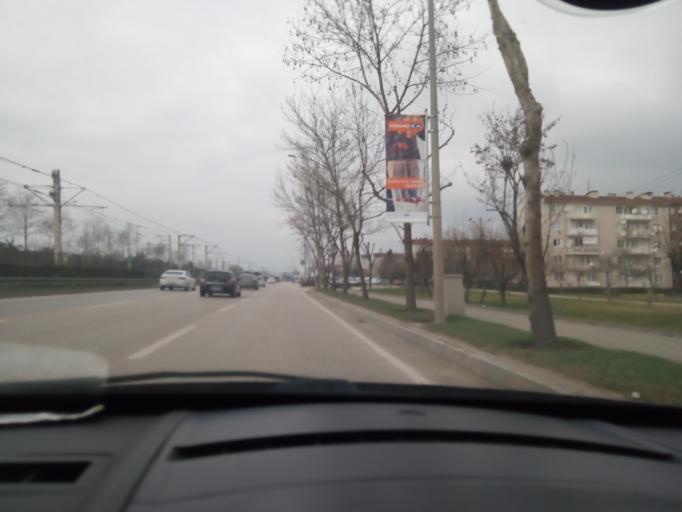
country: TR
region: Bursa
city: Niluefer
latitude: 40.2418
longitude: 28.9695
